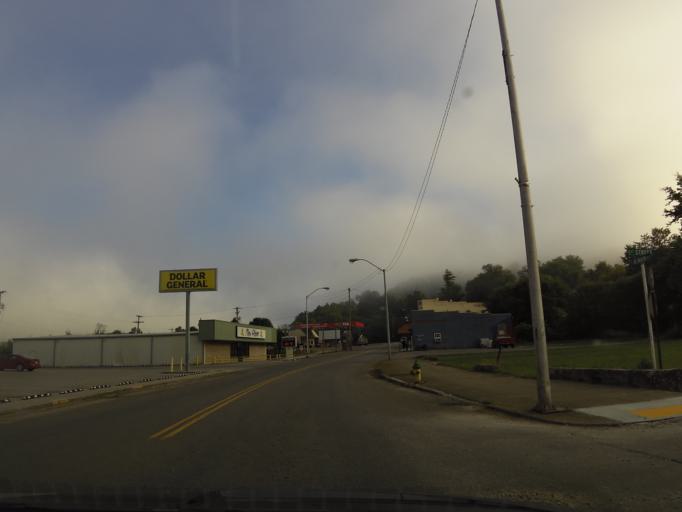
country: US
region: Tennessee
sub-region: Campbell County
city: Jellico
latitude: 36.5903
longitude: -84.1265
